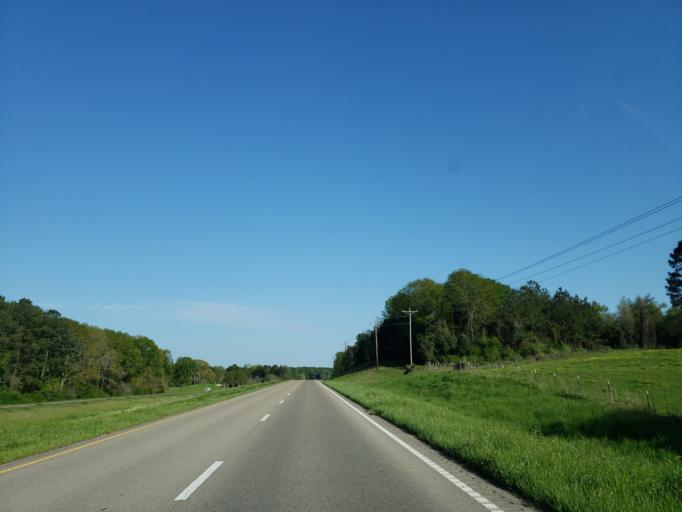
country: US
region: Mississippi
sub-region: Jones County
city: Ellisville
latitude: 31.6862
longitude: -89.3209
